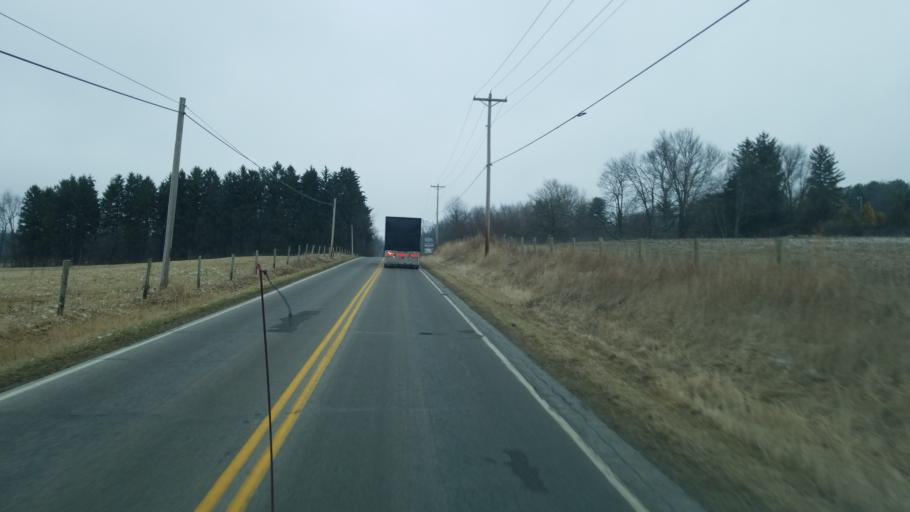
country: US
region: Ohio
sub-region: Wayne County
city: Apple Creek
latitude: 40.7636
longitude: -81.8438
